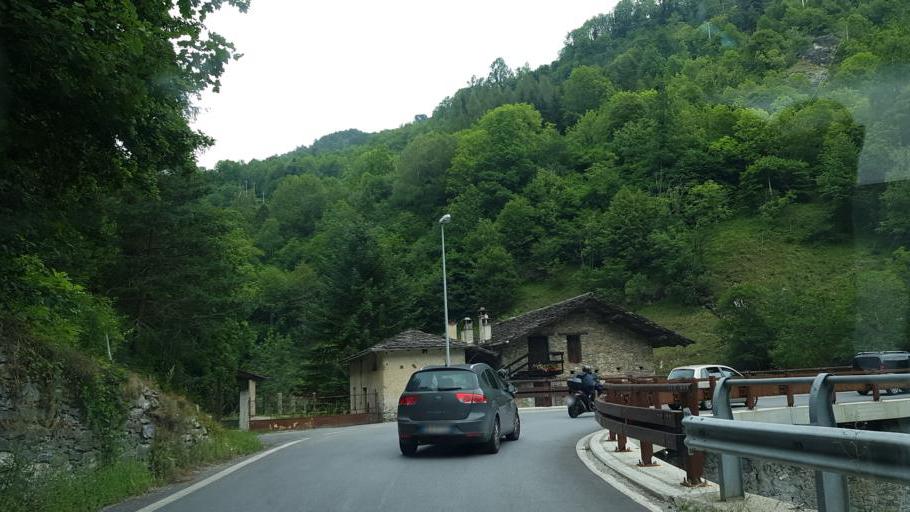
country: IT
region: Piedmont
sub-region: Provincia di Cuneo
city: Stroppo
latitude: 44.5037
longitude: 7.1224
